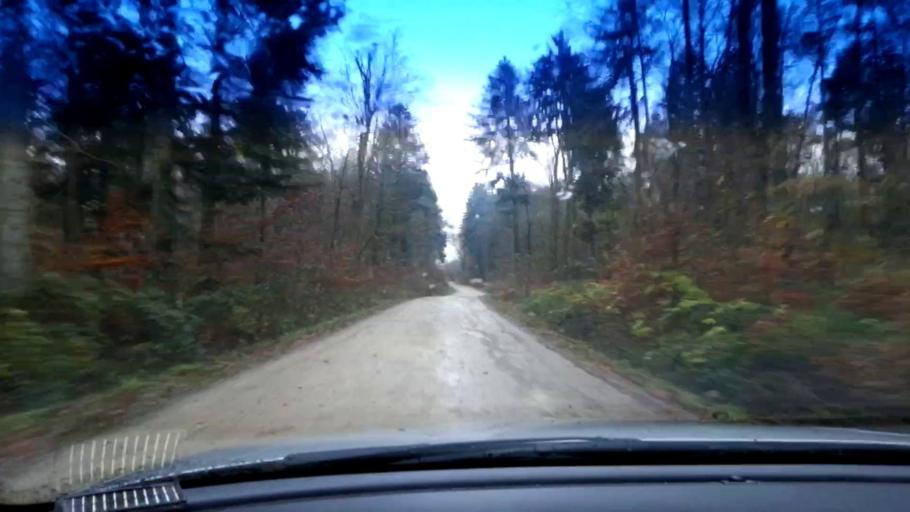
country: DE
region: Bavaria
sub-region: Upper Franconia
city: Schesslitz
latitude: 49.9572
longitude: 11.0333
